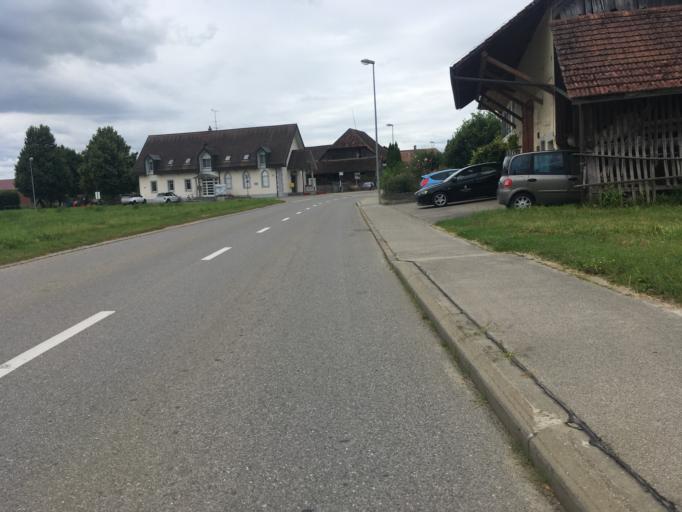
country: CH
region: Fribourg
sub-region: Broye District
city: Domdidier
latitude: 46.8789
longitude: 6.9683
